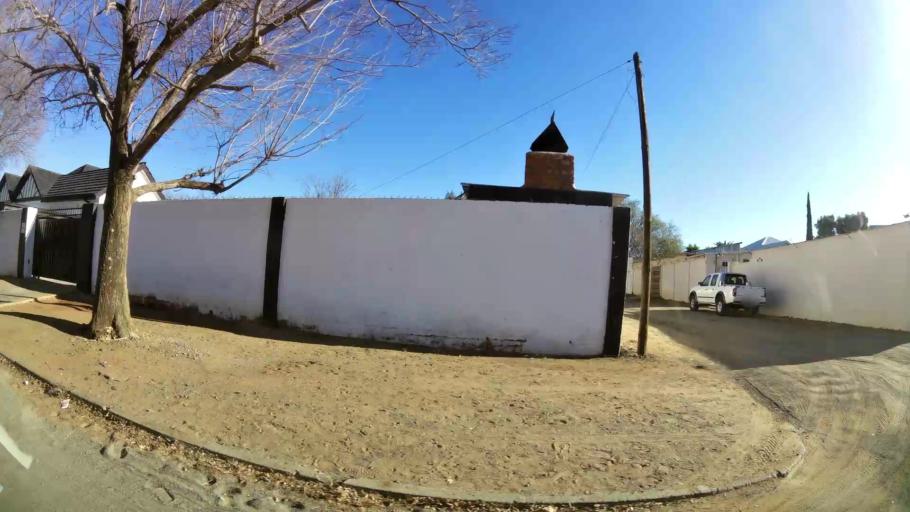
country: ZA
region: Northern Cape
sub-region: Frances Baard District Municipality
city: Kimberley
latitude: -28.7527
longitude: 24.7809
